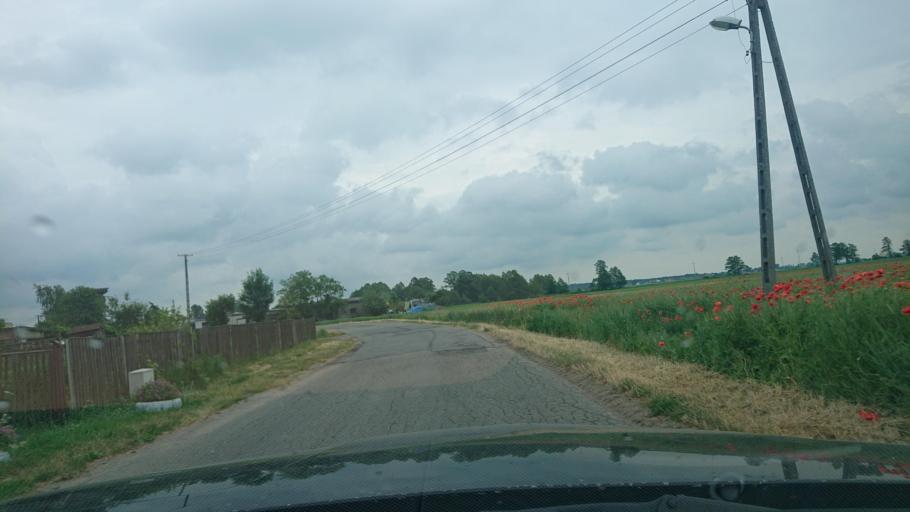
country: PL
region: Greater Poland Voivodeship
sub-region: Powiat gnieznienski
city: Gniezno
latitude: 52.4798
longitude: 17.5440
